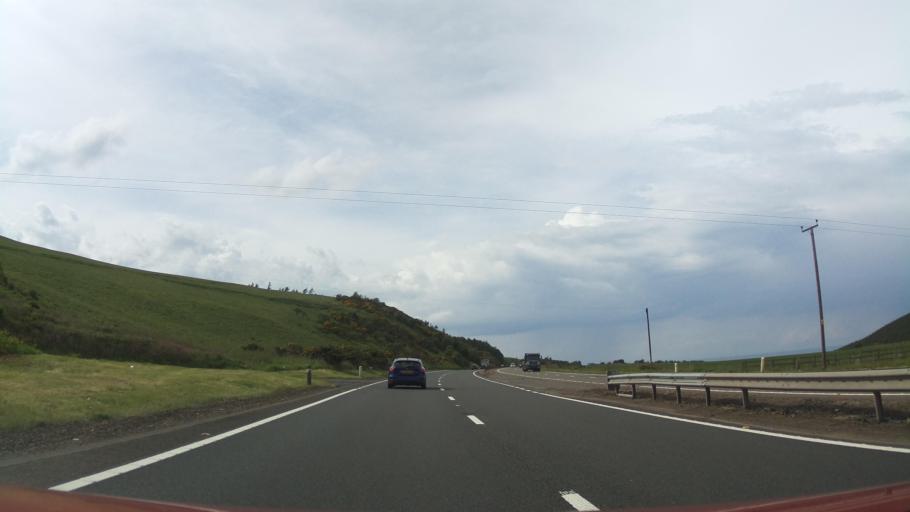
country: GB
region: Scotland
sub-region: The Scottish Borders
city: Duns
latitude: 55.9062
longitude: -2.3317
